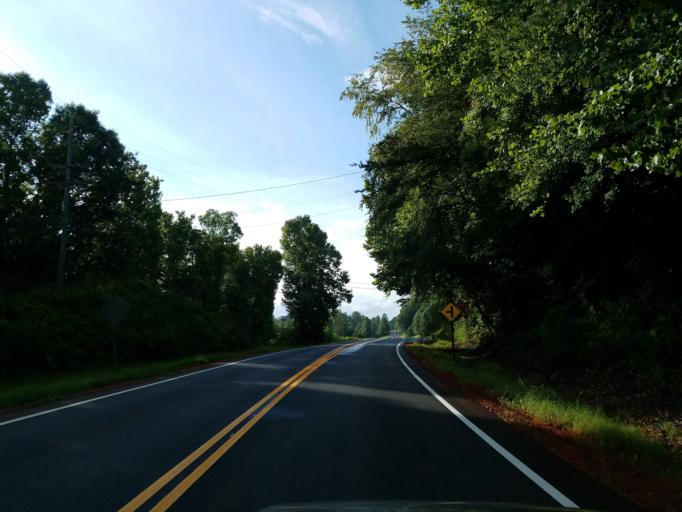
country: US
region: Georgia
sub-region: White County
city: Cleveland
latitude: 34.6145
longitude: -83.7944
